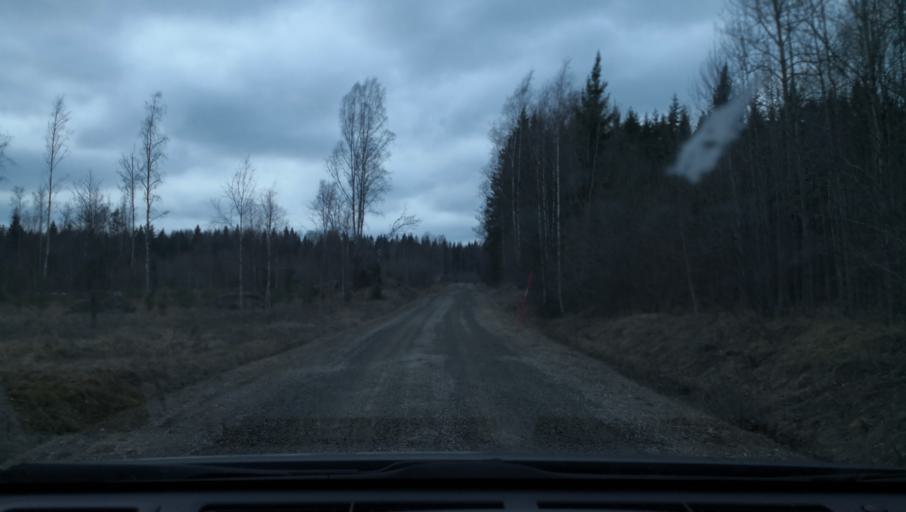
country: SE
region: OErebro
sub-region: Lindesbergs Kommun
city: Fellingsbro
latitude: 59.6007
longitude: 15.6184
